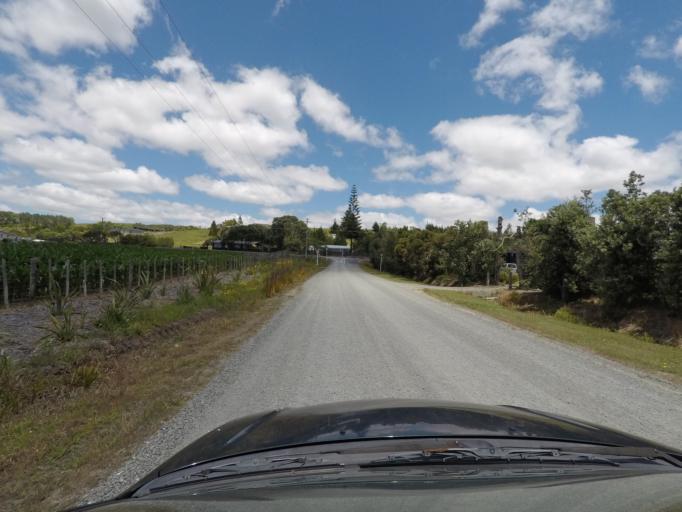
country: NZ
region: Northland
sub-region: Whangarei
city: Ruakaka
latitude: -35.9997
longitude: 174.4759
